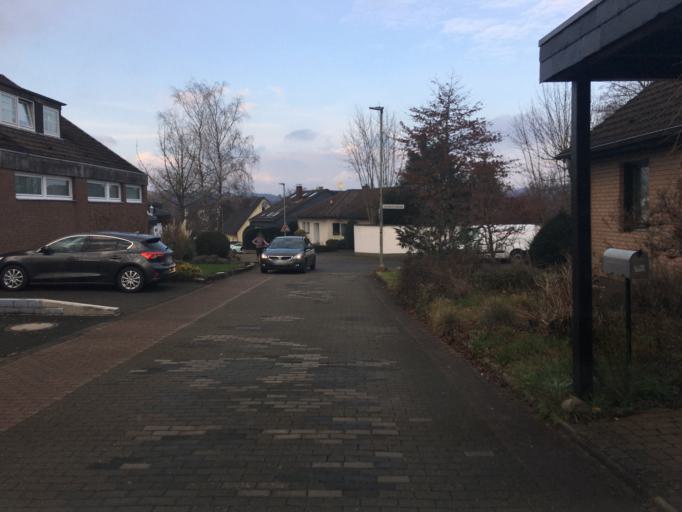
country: DE
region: North Rhine-Westphalia
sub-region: Regierungsbezirk Koln
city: Odenthal
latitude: 51.0206
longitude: 7.1003
